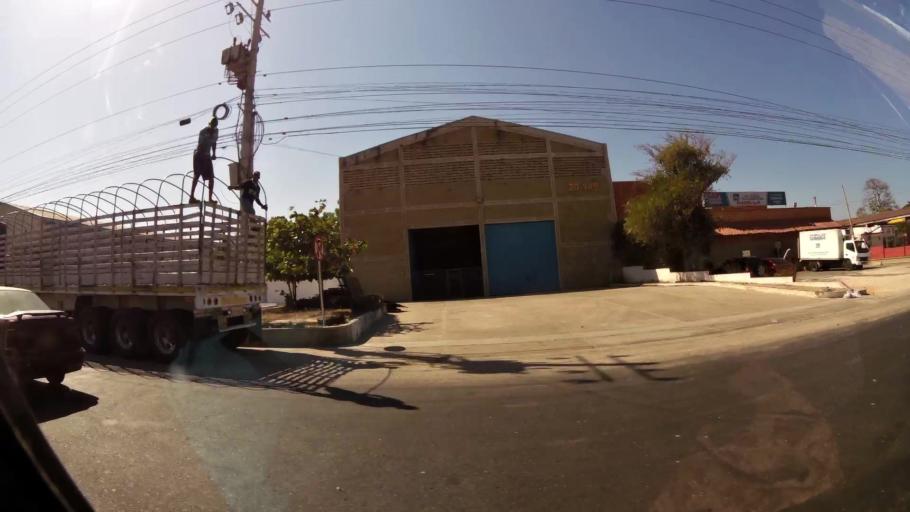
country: CO
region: Atlantico
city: Barranquilla
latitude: 10.9581
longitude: -74.7856
